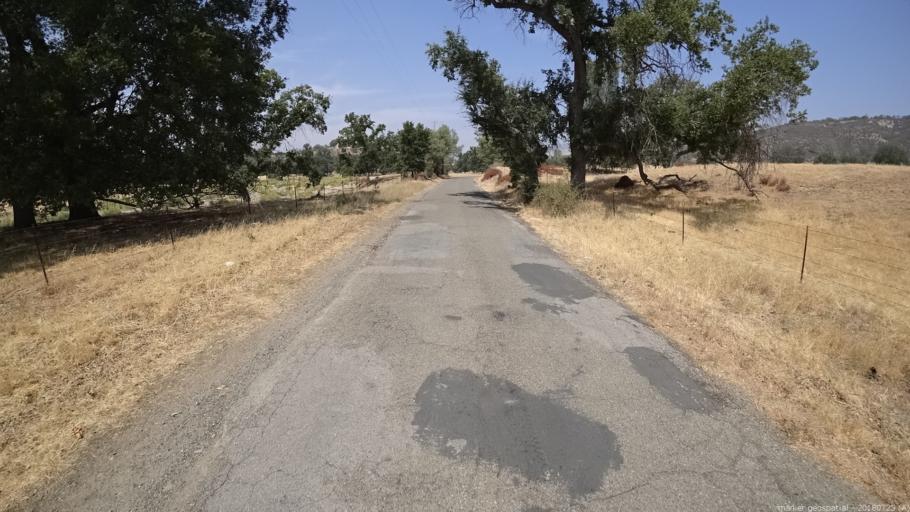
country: US
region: California
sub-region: Fresno County
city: Coalinga
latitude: 35.9310
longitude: -120.4585
